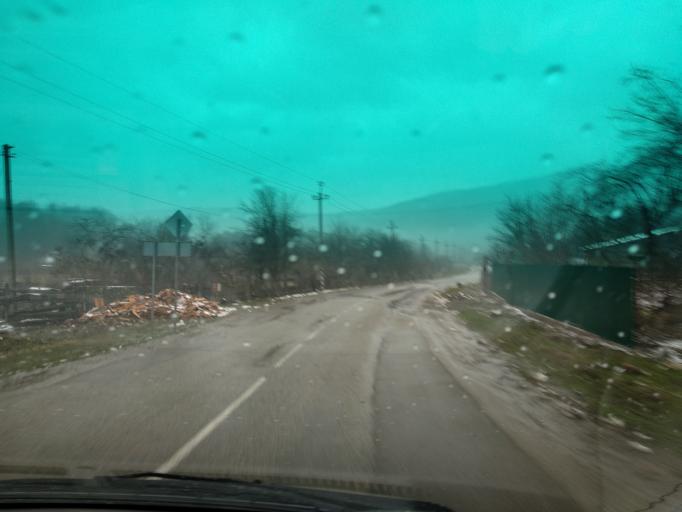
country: RU
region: Krasnodarskiy
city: Khadyzhensk
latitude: 44.2363
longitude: 39.3795
